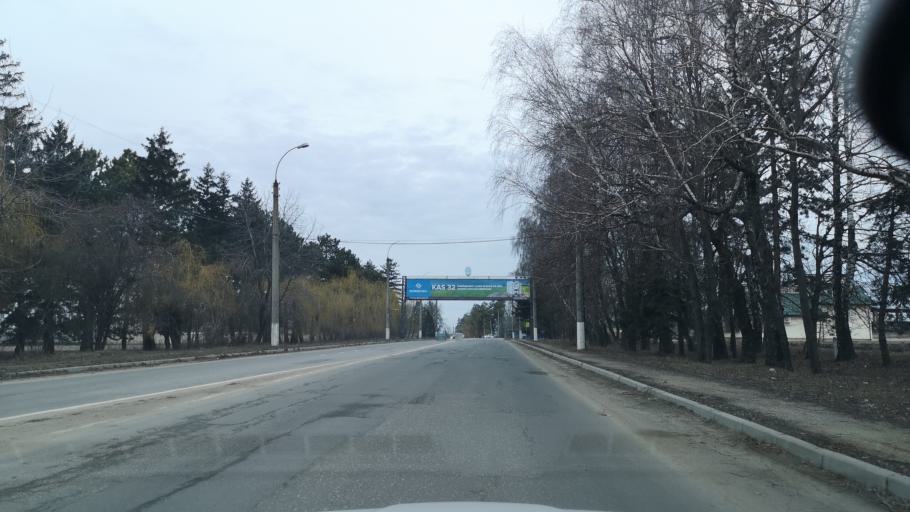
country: MD
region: Raionul Edinet
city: Edinet
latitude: 48.1596
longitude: 27.3293
